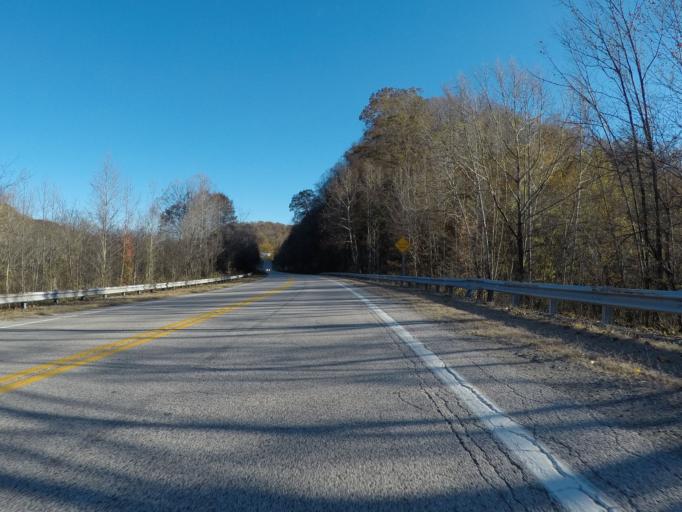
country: US
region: West Virginia
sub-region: Wayne County
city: Ceredo
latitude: 38.3790
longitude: -82.5626
